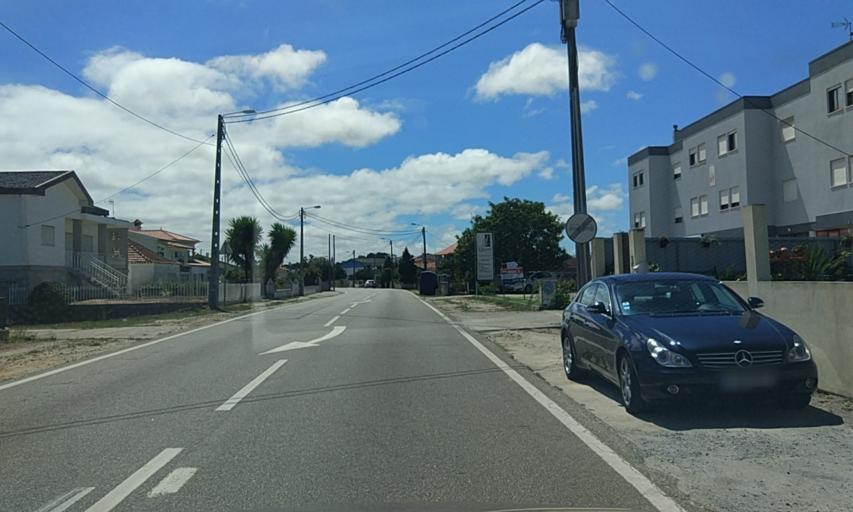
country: PT
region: Aveiro
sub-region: Vagos
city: Vagos
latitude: 40.5297
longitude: -8.6789
